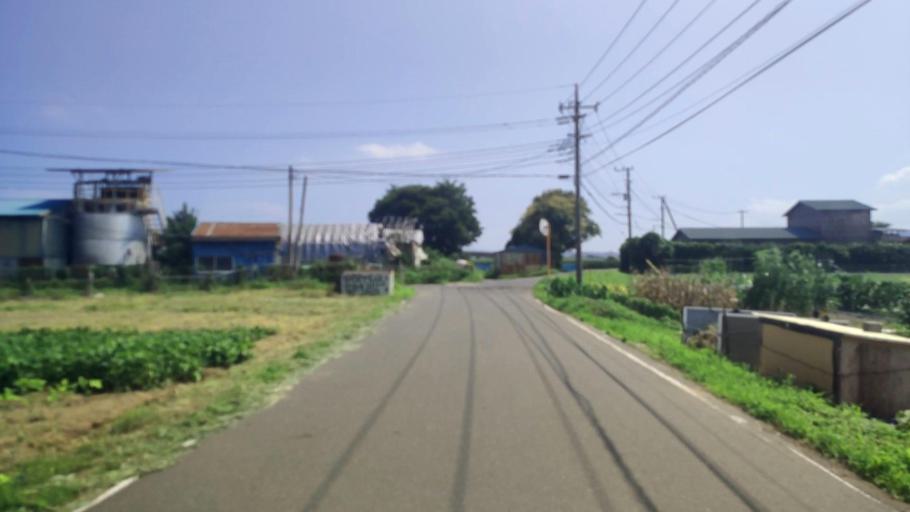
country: JP
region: Kanagawa
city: Isehara
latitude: 35.3682
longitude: 139.3072
